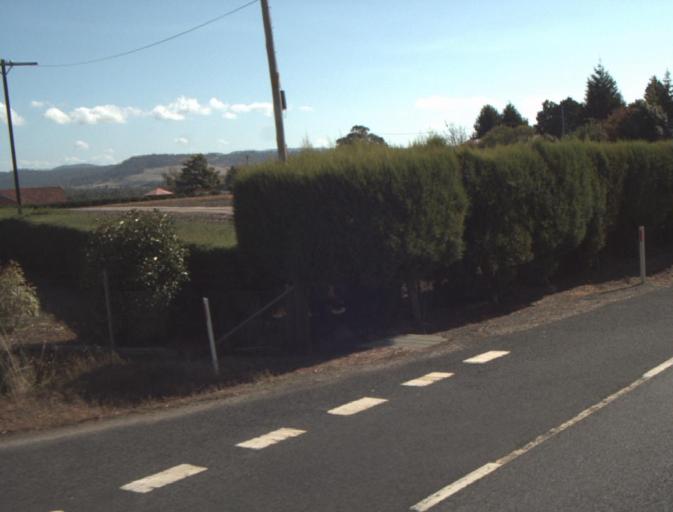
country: AU
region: Tasmania
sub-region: Launceston
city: Mayfield
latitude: -41.3406
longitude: 147.0869
